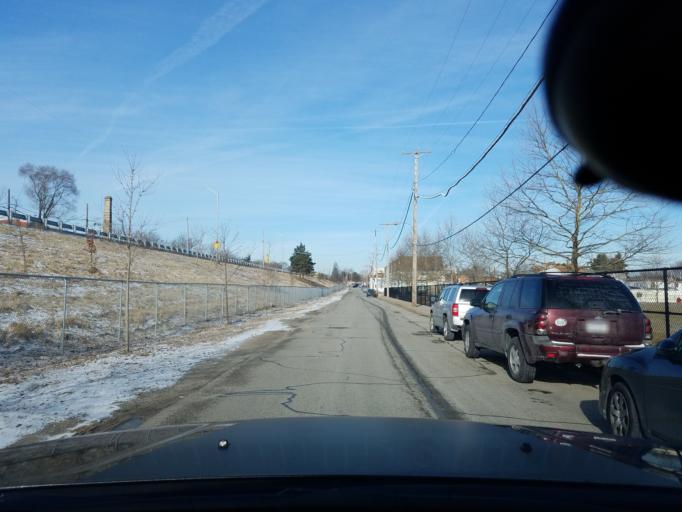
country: US
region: Pennsylvania
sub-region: Allegheny County
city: Wilkinsburg
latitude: 40.4514
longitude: -79.8944
